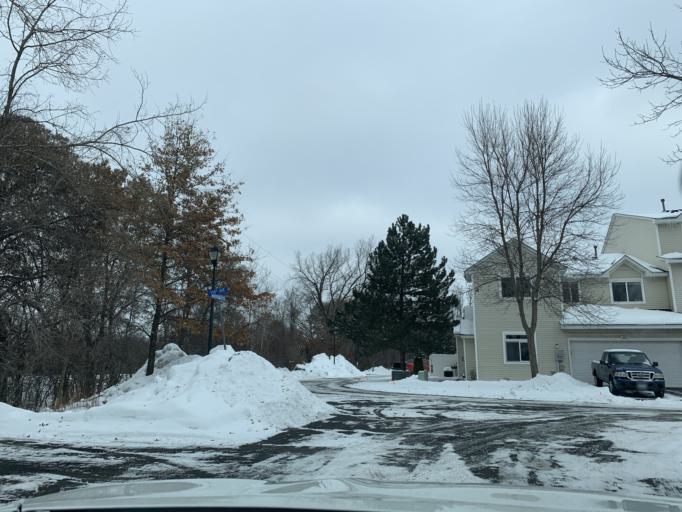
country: US
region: Minnesota
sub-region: Anoka County
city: Coon Rapids
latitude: 45.1664
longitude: -93.2935
